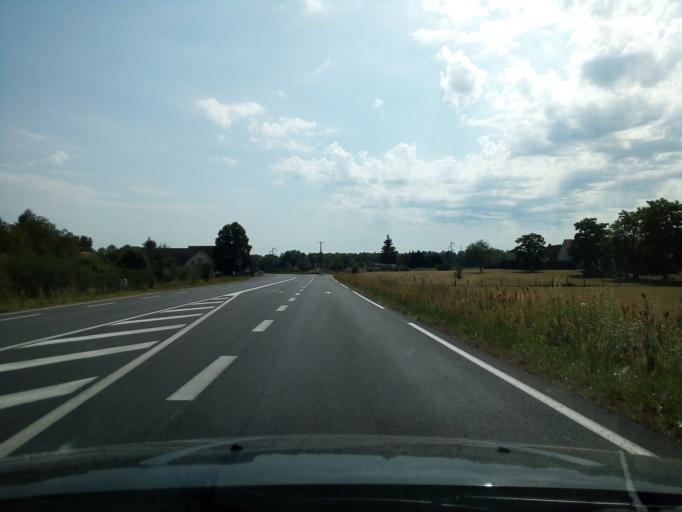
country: FR
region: Auvergne
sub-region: Departement de l'Allier
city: Varennes-sur-Allier
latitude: 46.3200
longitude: 3.3566
